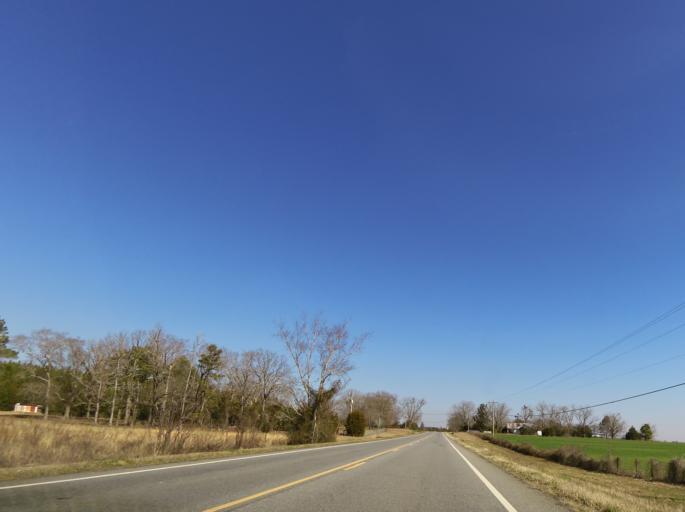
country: US
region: Georgia
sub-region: Bleckley County
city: Cochran
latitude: 32.3422
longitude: -83.3993
